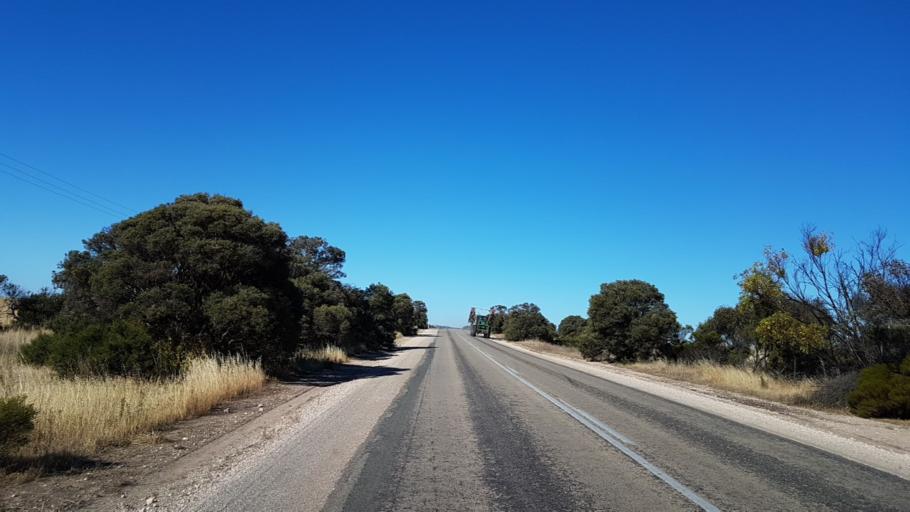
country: AU
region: South Australia
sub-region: Yorke Peninsula
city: Honiton
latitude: -34.8497
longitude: 137.5159
